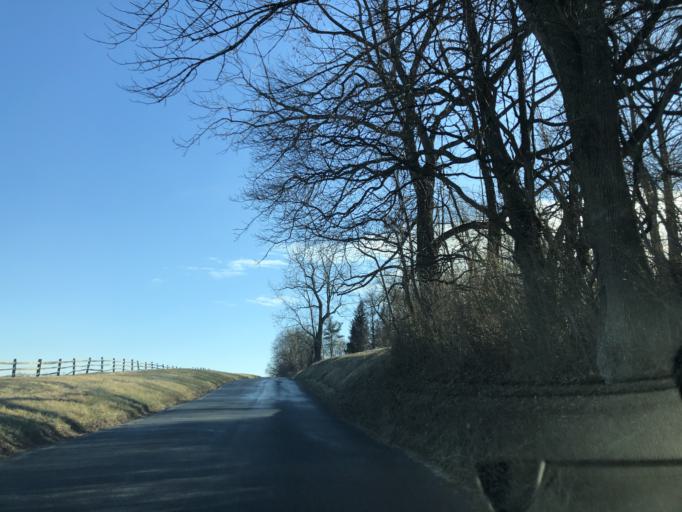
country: US
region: Pennsylvania
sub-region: Chester County
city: Upland
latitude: 39.8964
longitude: -75.7808
